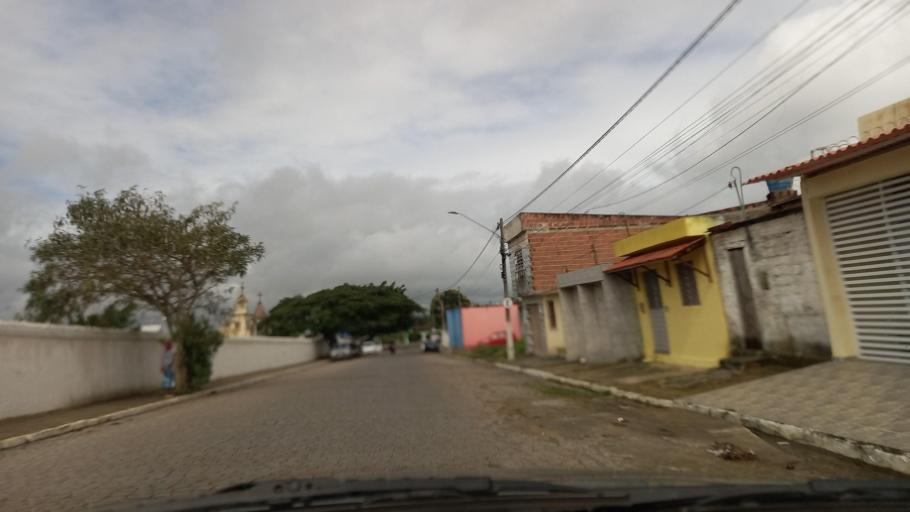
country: BR
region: Pernambuco
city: Garanhuns
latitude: -8.9055
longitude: -36.4971
